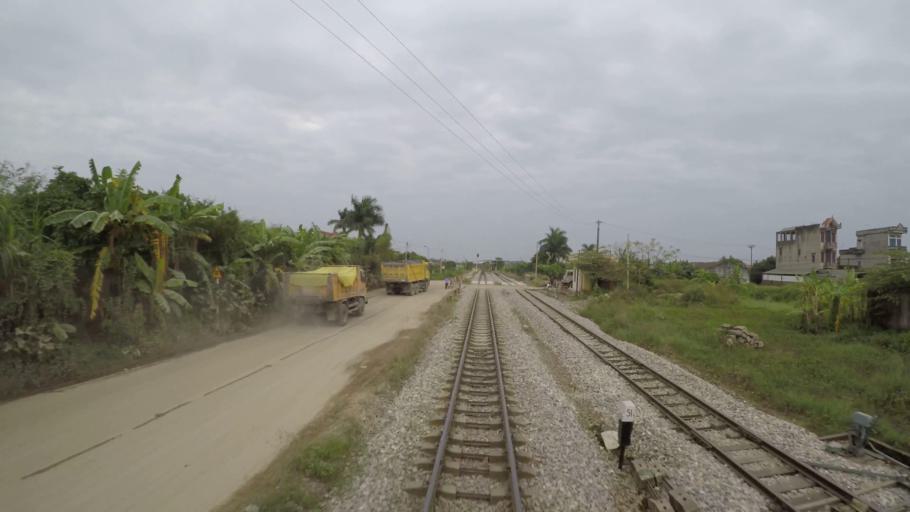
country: VN
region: Hai Duong
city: Lai Cach
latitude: 20.9487
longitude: 106.2522
